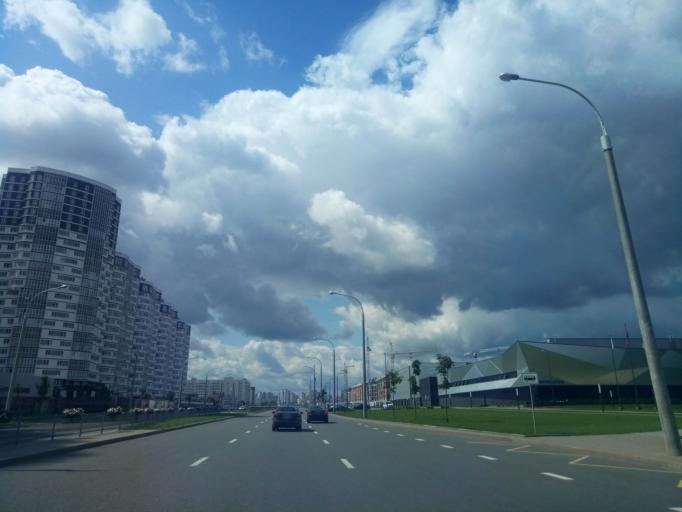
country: BY
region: Minsk
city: Zhdanovichy
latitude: 53.9440
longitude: 27.4605
